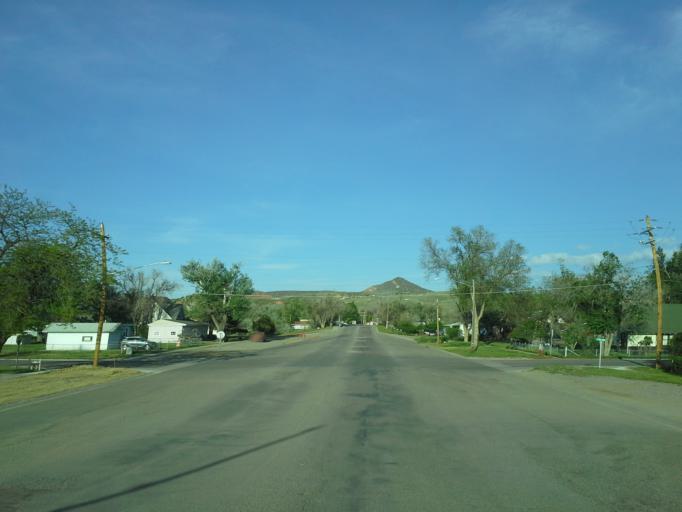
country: US
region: Wyoming
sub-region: Hot Springs County
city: Thermopolis
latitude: 43.6461
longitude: -108.2057
